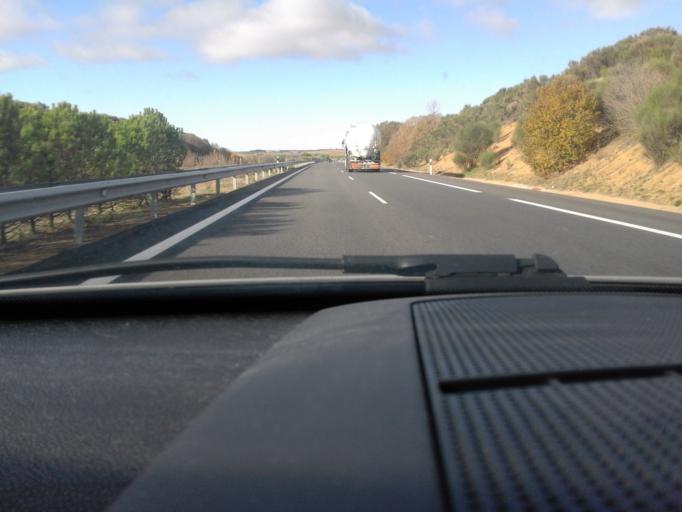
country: ES
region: Castille and Leon
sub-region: Provincia de Palencia
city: Moratinos
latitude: 42.3642
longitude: -4.9364
